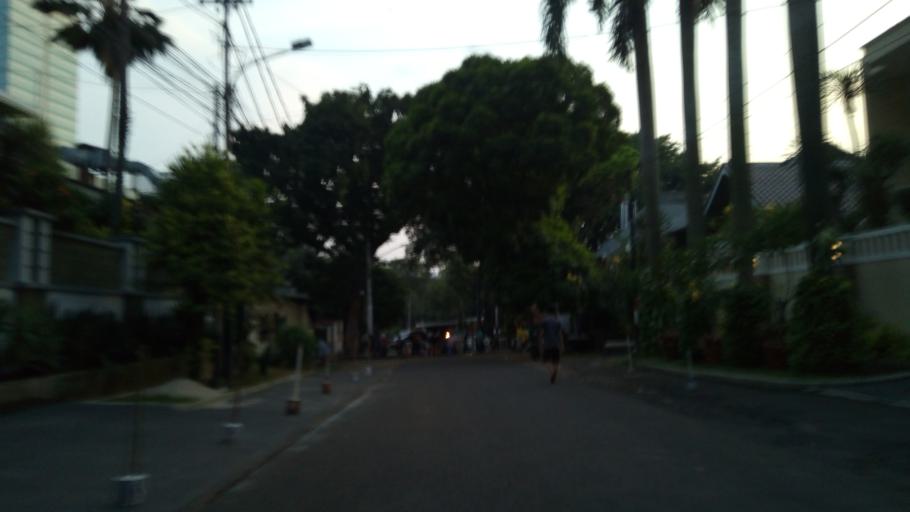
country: ID
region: Jakarta Raya
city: Jakarta
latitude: -6.2441
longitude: 106.7952
